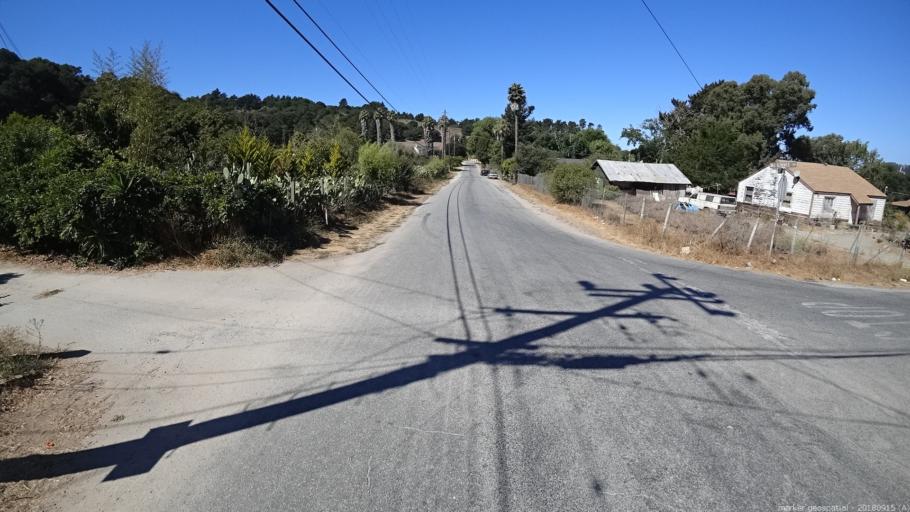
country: US
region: California
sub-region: Monterey County
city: Las Lomas
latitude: 36.8537
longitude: -121.7063
